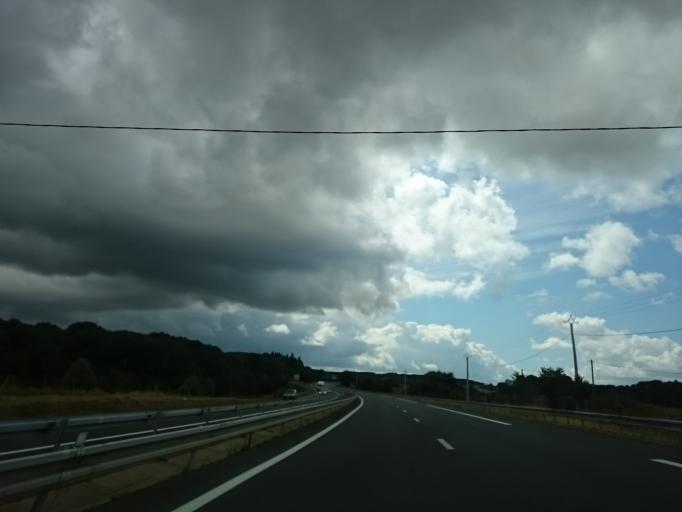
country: FR
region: Pays de la Loire
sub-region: Departement de la Sarthe
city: La Chapelle-Saint-Aubin
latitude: 48.0306
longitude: 0.1351
